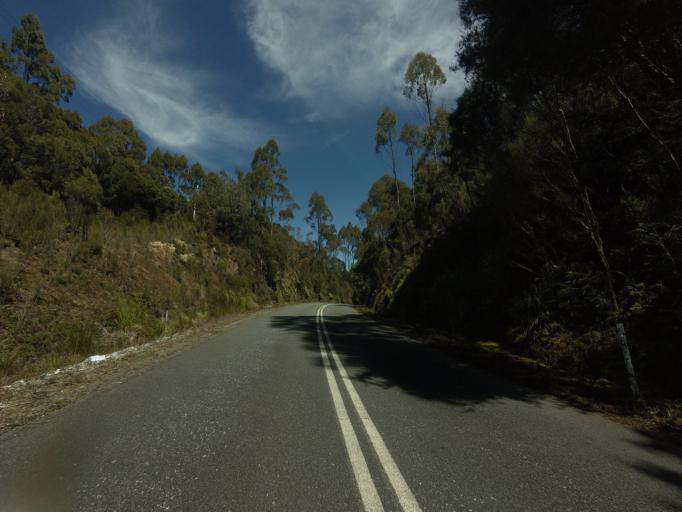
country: AU
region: Tasmania
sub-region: West Coast
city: Queenstown
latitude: -42.7732
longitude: 146.0422
